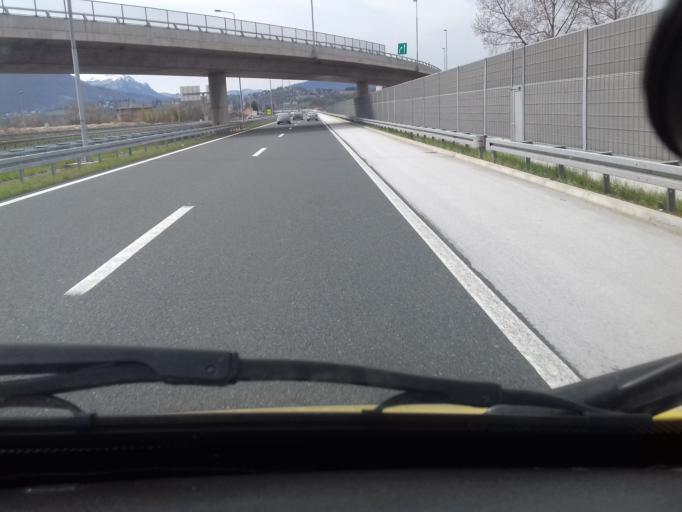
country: BA
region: Federation of Bosnia and Herzegovina
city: Vogosca
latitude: 43.8748
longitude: 18.2918
